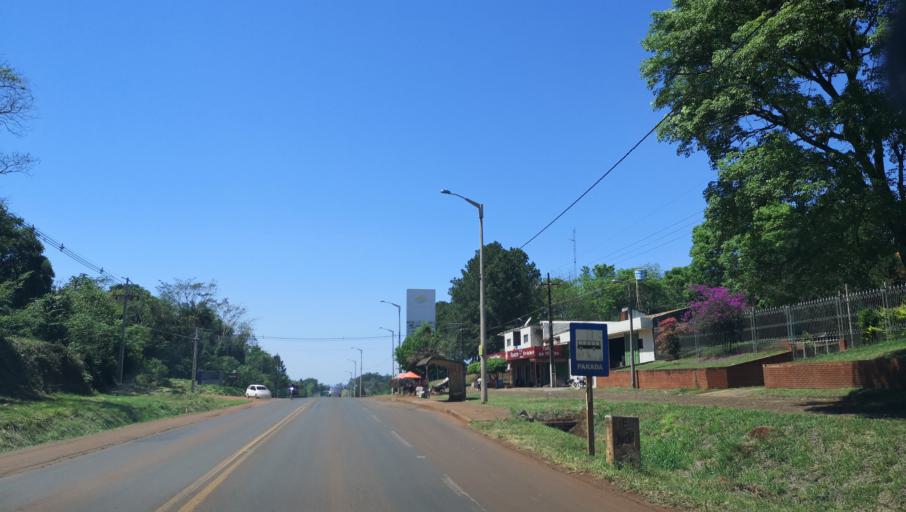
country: PY
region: Itapua
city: San Juan del Parana
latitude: -27.2807
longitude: -55.9453
